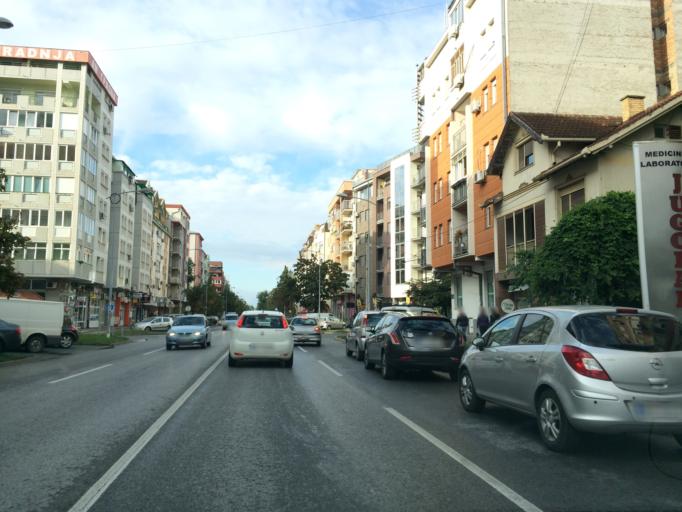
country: RS
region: Autonomna Pokrajina Vojvodina
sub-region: Juznobacki Okrug
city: Novi Sad
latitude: 45.2408
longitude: 19.8253
